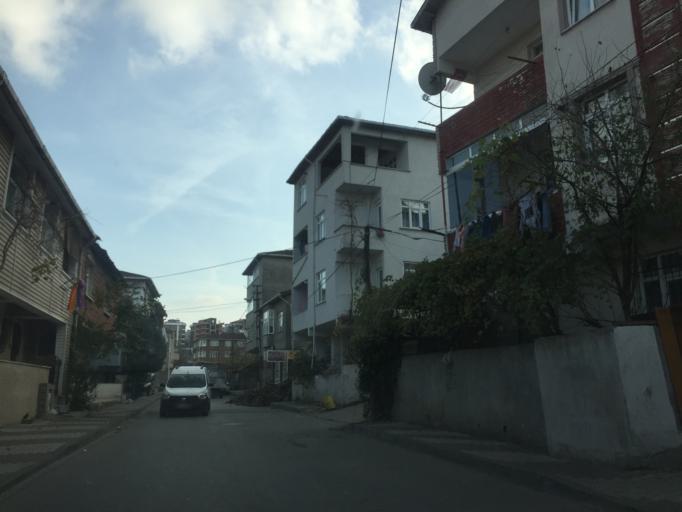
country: TR
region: Istanbul
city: Sultanbeyli
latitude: 40.9447
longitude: 29.2977
